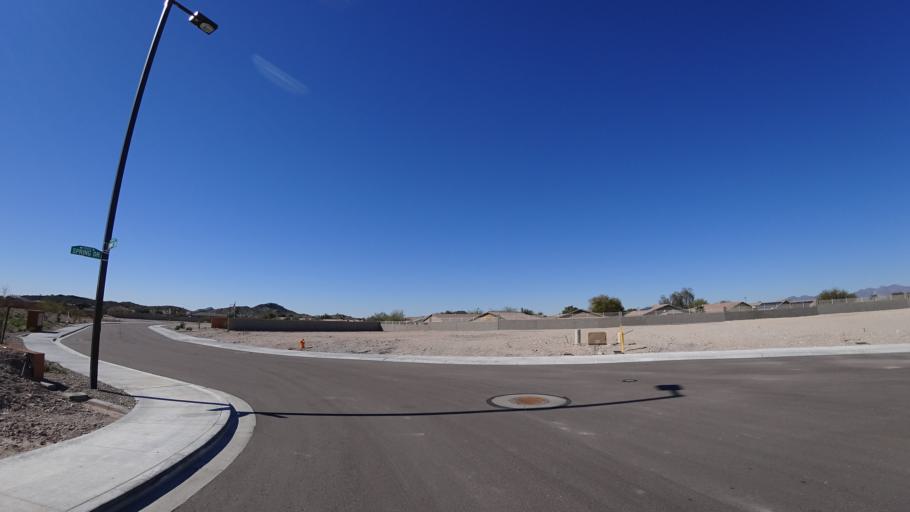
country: US
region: Arizona
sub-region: Maricopa County
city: Goodyear
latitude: 33.3498
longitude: -112.4243
